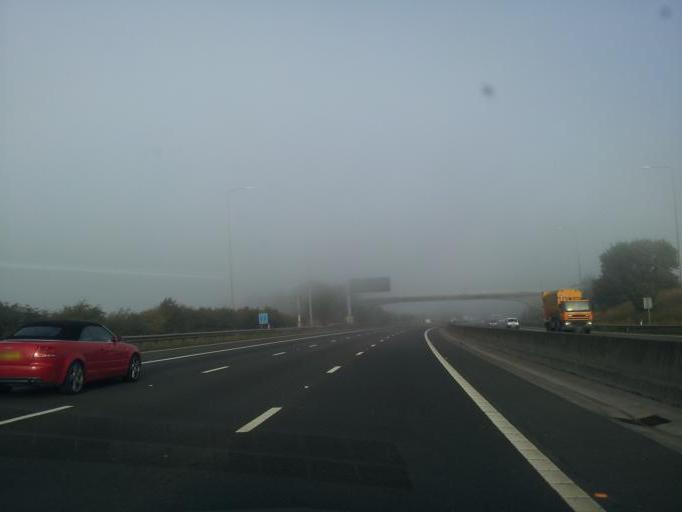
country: GB
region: England
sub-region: City and Borough of Leeds
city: Morley
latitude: 53.7352
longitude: -1.6177
